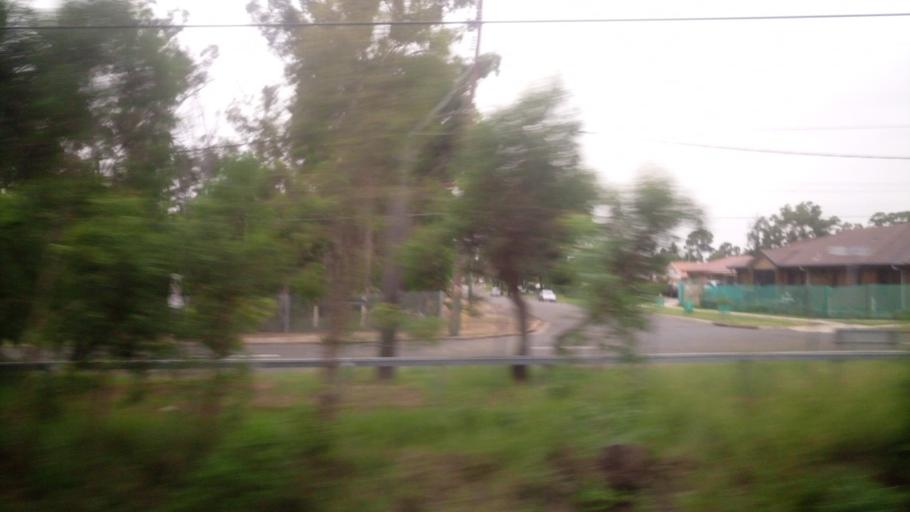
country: AU
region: New South Wales
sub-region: Blacktown
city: Doonside
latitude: -33.7646
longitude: 150.8852
